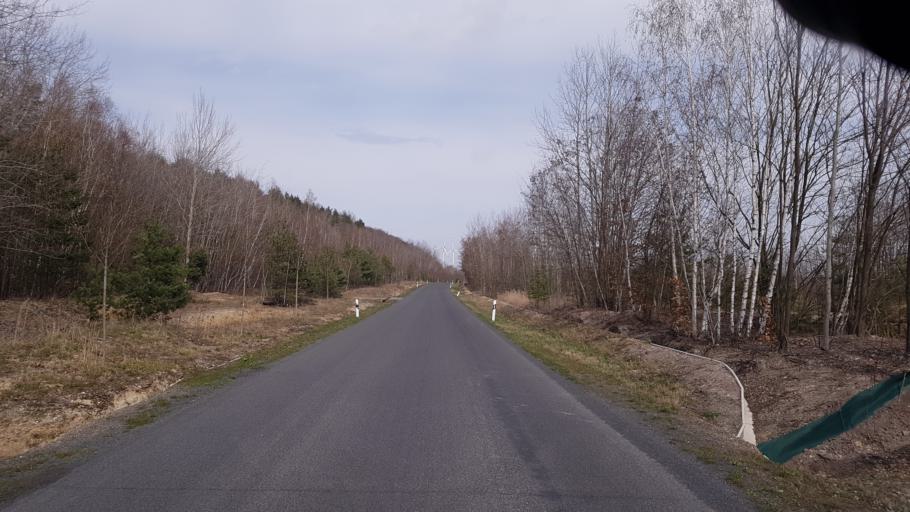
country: DE
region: Brandenburg
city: Schipkau
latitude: 51.5273
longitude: 13.8430
